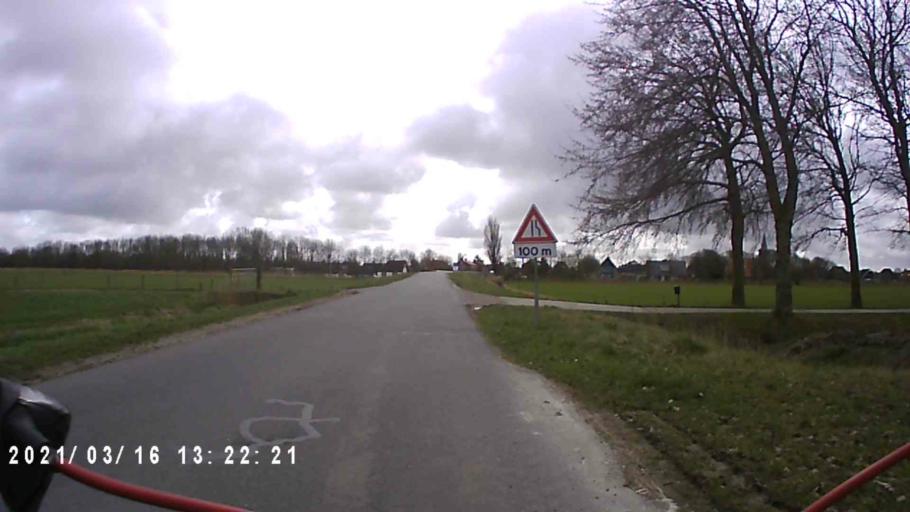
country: NL
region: Friesland
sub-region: Gemeente Het Bildt
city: Minnertsga
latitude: 53.2261
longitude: 5.5891
